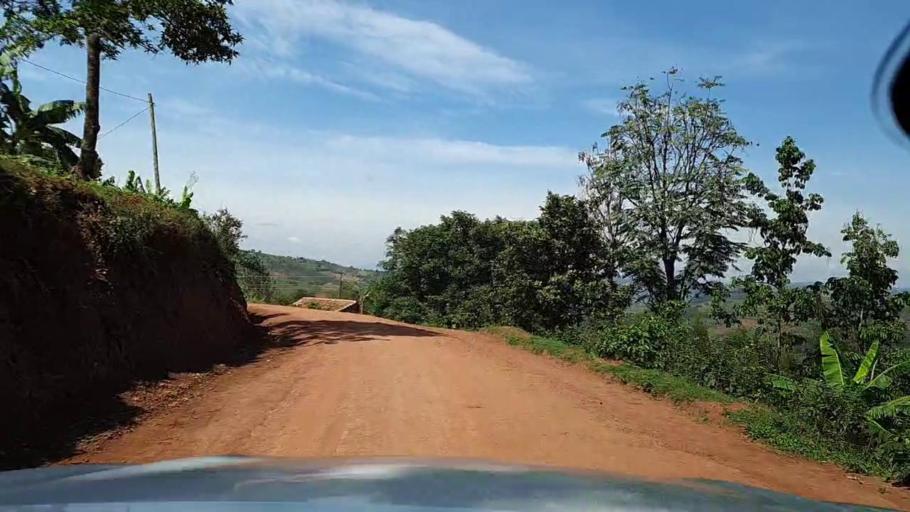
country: RW
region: Southern Province
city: Butare
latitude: -2.6920
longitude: 29.8544
